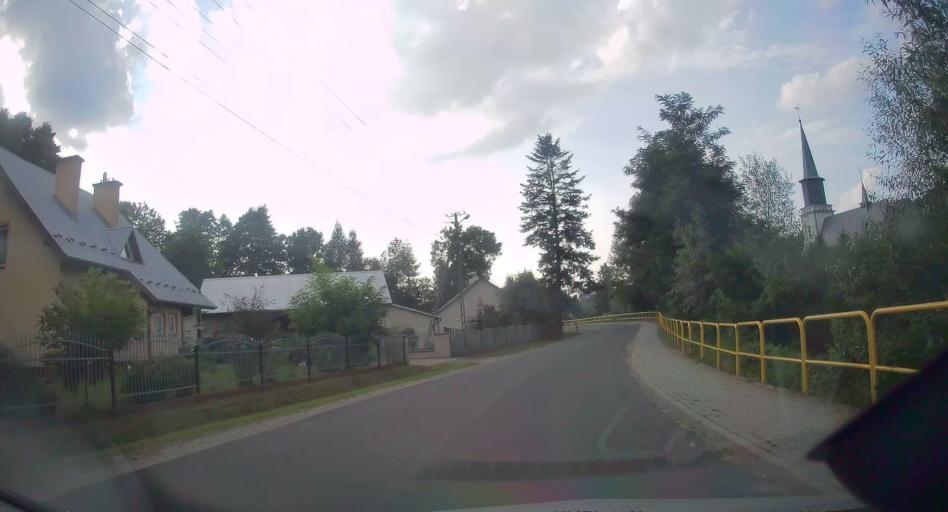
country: PL
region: Subcarpathian Voivodeship
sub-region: Powiat debicki
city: Debica
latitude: 49.9942
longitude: 21.4214
